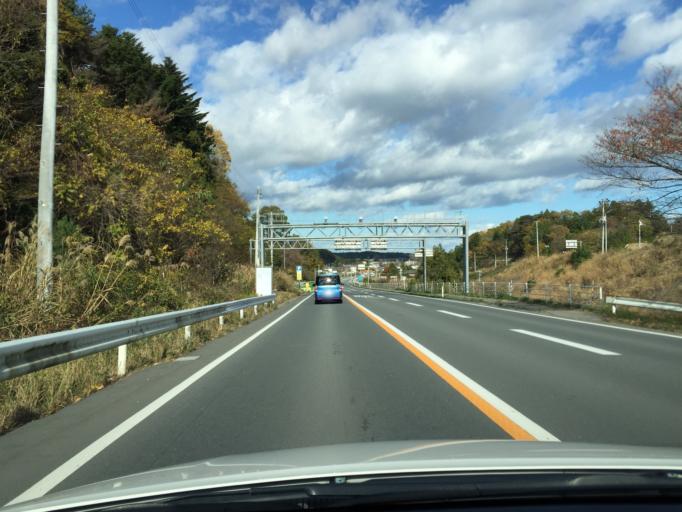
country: JP
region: Fukushima
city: Namie
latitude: 37.4404
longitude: 141.0102
